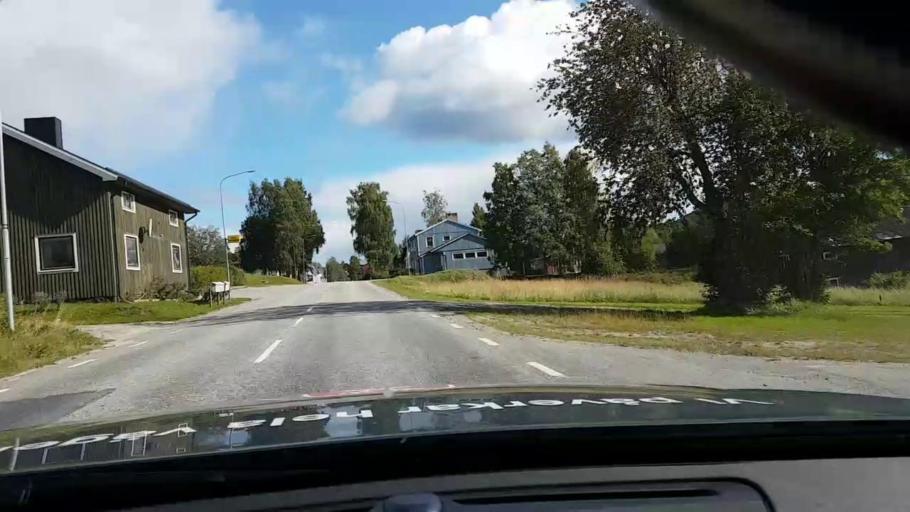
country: SE
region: Vaesterbotten
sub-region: Asele Kommun
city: Asele
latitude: 63.7898
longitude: 17.6360
